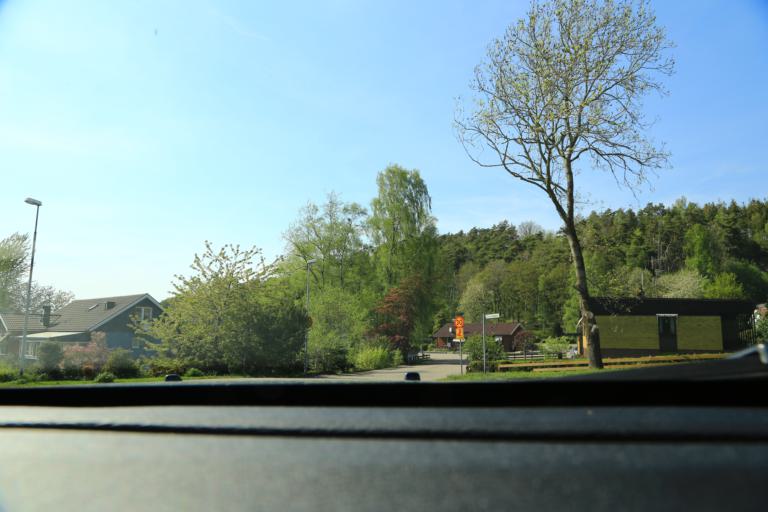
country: SE
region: Halland
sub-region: Varbergs Kommun
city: Varberg
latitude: 57.1420
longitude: 12.2906
